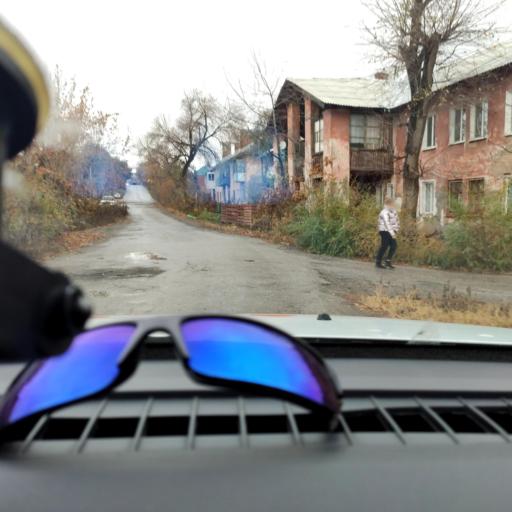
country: RU
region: Samara
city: Samara
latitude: 53.1726
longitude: 50.1733
